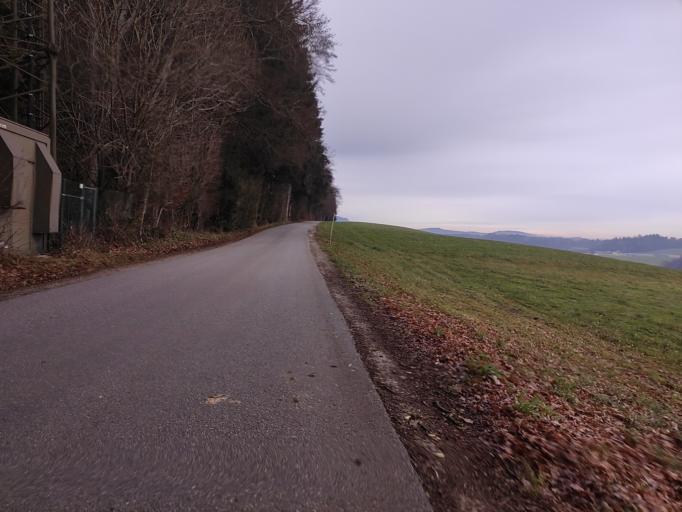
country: AT
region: Salzburg
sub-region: Politischer Bezirk Salzburg-Umgebung
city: Obertrum am See
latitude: 47.9070
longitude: 13.0653
